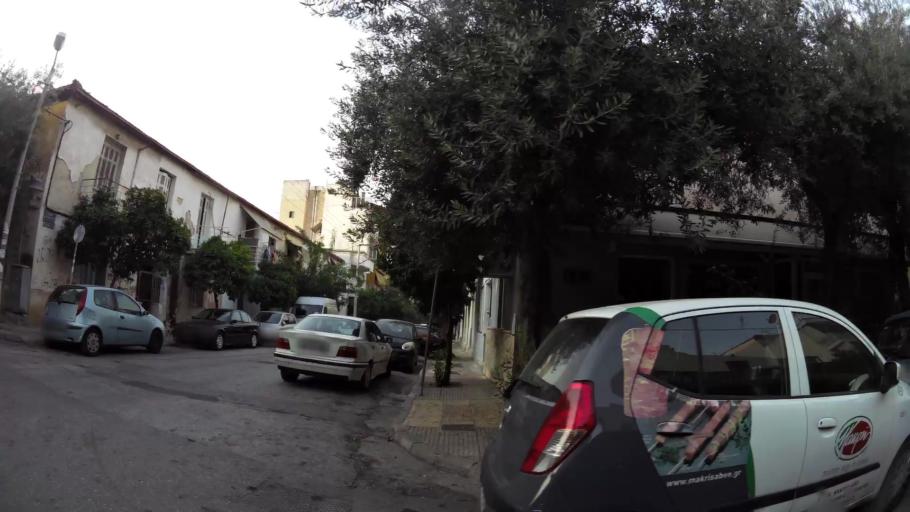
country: GR
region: Attica
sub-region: Nomarchia Athinas
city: Kallithea
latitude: 37.9528
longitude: 23.7037
